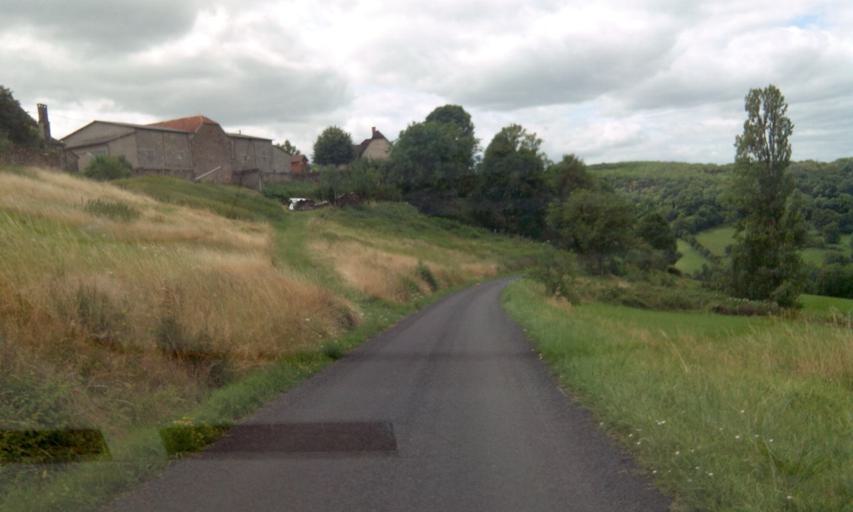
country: FR
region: Limousin
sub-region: Departement de la Correze
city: Cosnac
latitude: 45.0772
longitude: 1.5816
